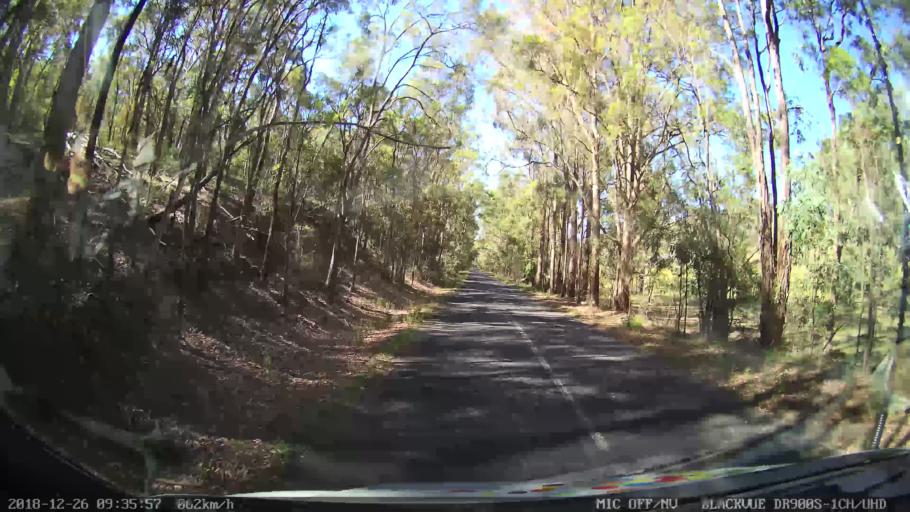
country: AU
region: New South Wales
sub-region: Mid-Western Regional
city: Kandos
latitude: -32.9196
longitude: 150.0412
